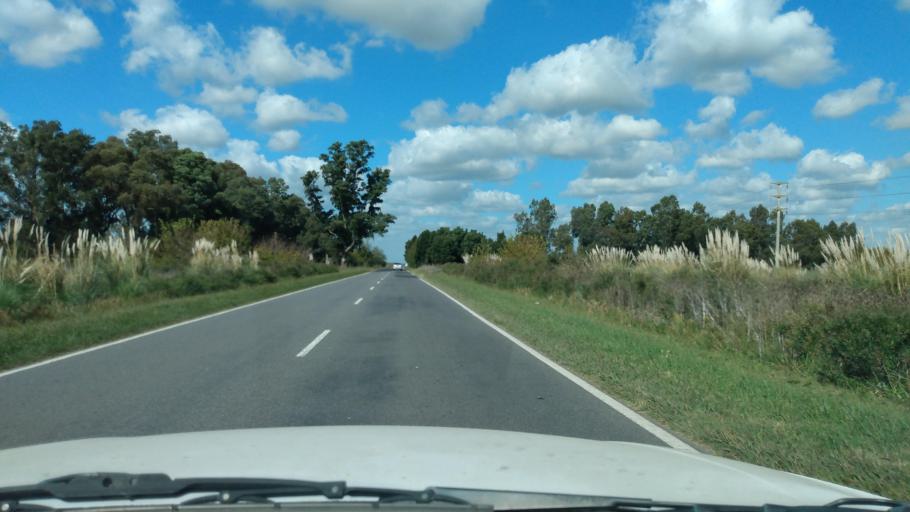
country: AR
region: Buenos Aires
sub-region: Partido de Navarro
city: Navarro
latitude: -34.8853
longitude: -59.3395
